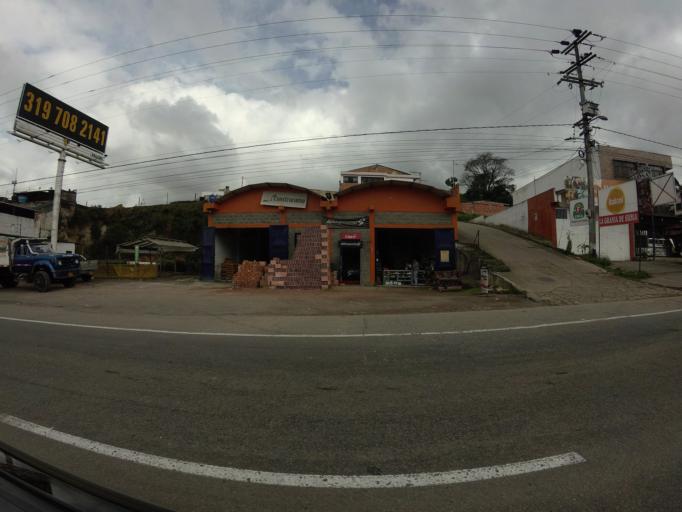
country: CO
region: Cundinamarca
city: Silvania
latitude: 4.4704
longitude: -74.3842
